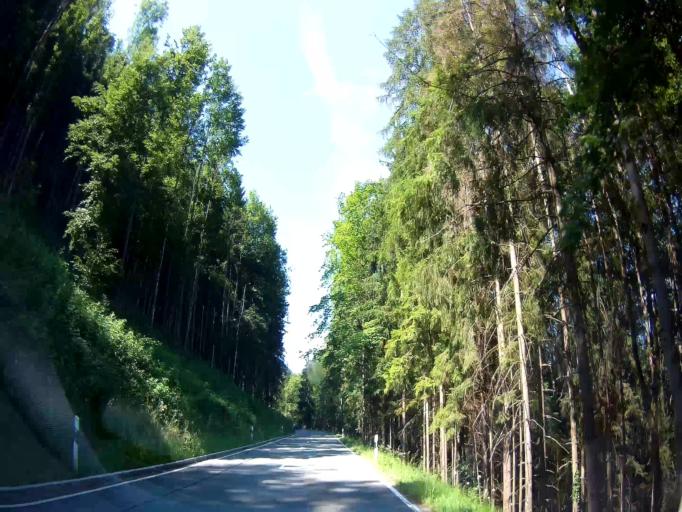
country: DE
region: Bavaria
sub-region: Upper Bavaria
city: Berchtesgaden
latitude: 47.6386
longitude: 13.0556
